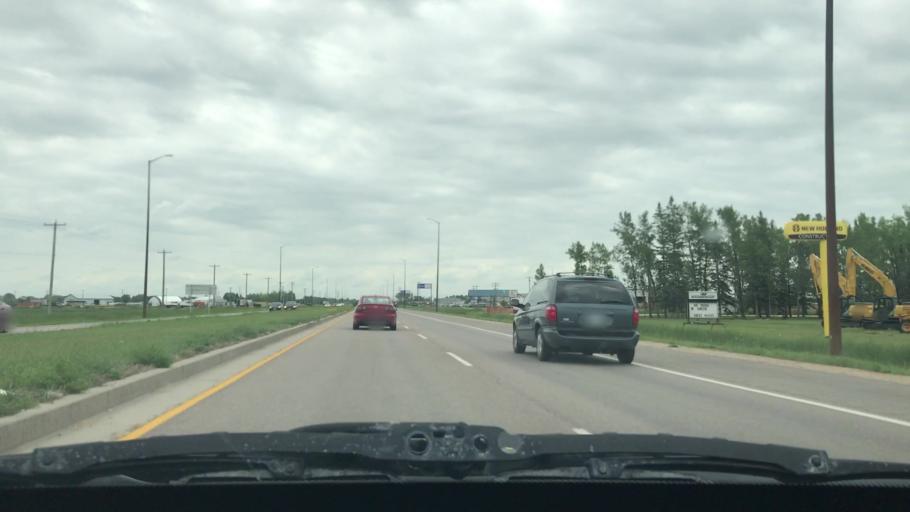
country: CA
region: Manitoba
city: Winnipeg
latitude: 49.8507
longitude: -97.0020
